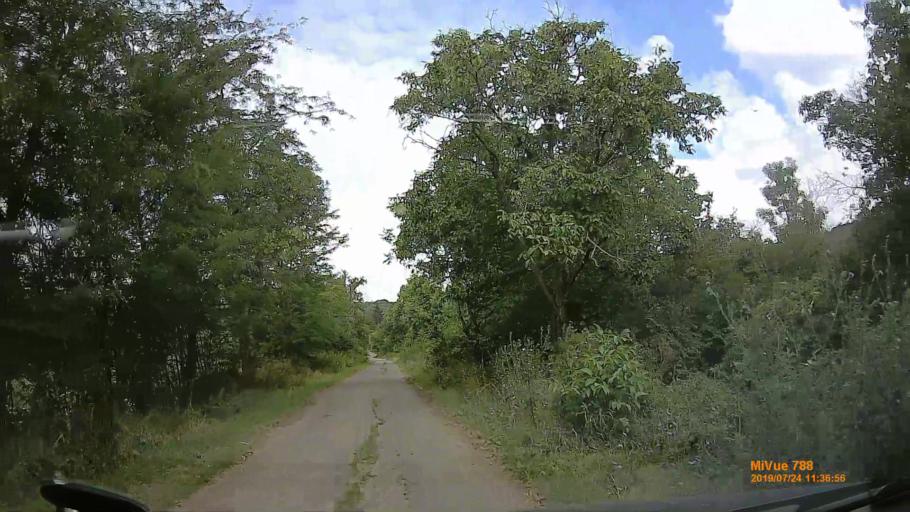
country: UA
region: Zakarpattia
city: Batiovo
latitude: 48.2408
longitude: 22.4762
